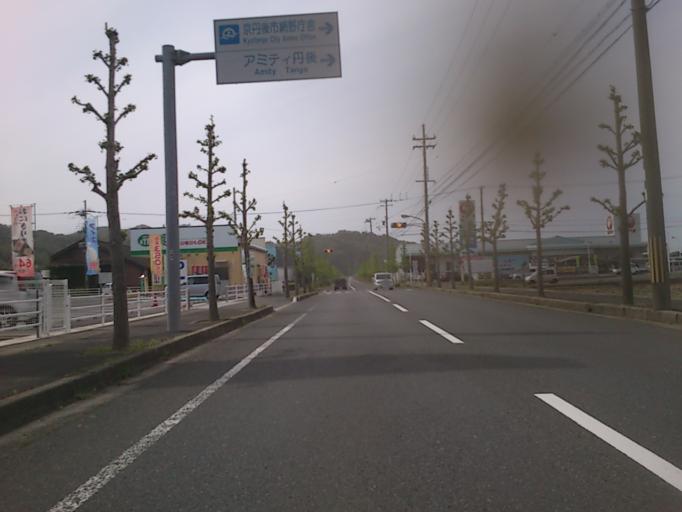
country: JP
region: Kyoto
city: Miyazu
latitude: 35.6789
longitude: 135.0239
